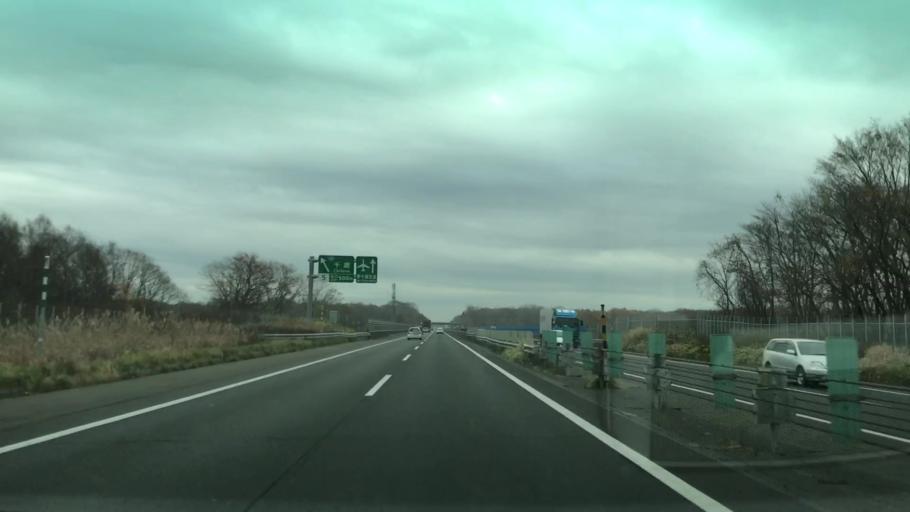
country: JP
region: Hokkaido
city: Chitose
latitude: 42.8205
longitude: 141.6175
